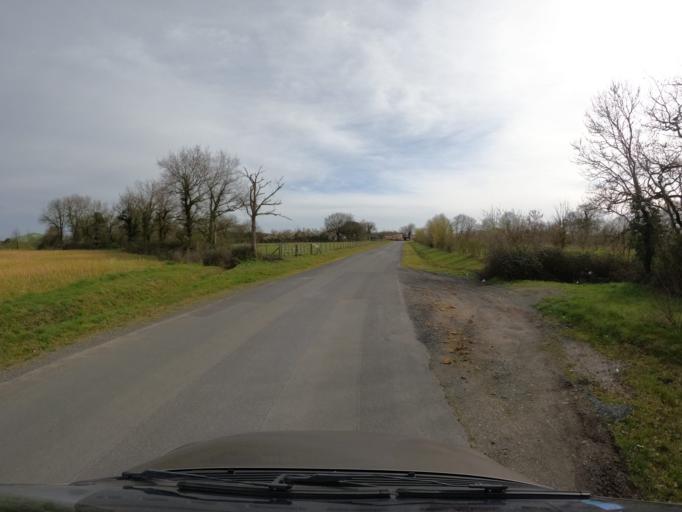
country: FR
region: Pays de la Loire
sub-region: Departement de la Vendee
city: Bouffere
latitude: 46.9672
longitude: -1.3303
